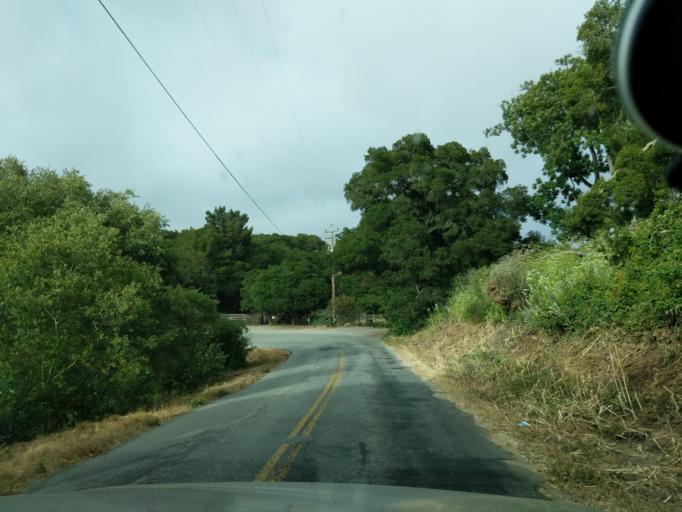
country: US
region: California
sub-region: Monterey County
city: Elkhorn
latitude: 36.8203
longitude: -121.7275
